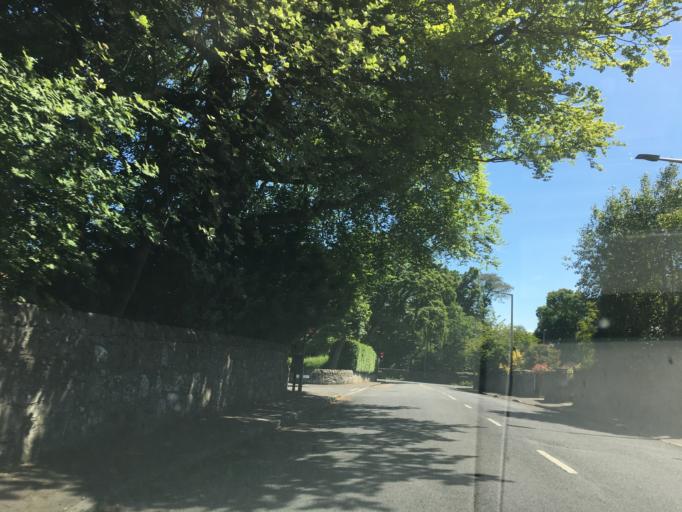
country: GB
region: Scotland
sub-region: Fife
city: Aberdour
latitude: 55.9734
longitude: -3.2958
